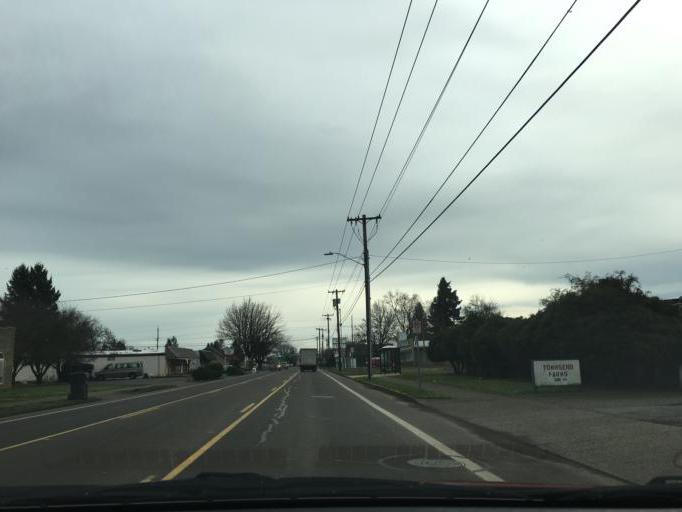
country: US
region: Oregon
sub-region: Marion County
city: Woodburn
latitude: 45.1382
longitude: -122.8470
